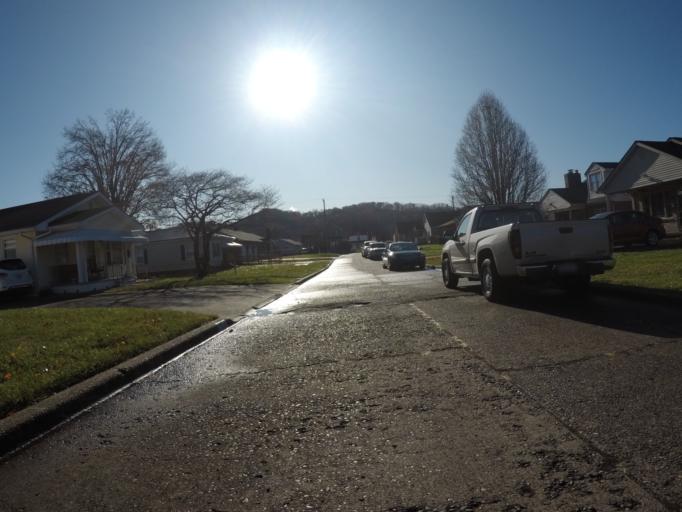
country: US
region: Ohio
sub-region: Lawrence County
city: Burlington
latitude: 38.4029
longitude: -82.5147
